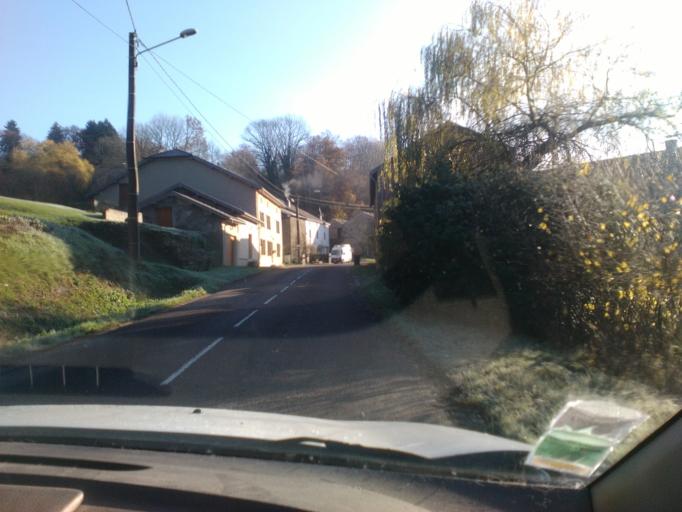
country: FR
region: Lorraine
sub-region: Departement des Vosges
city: Uzemain
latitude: 48.0637
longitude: 6.3301
